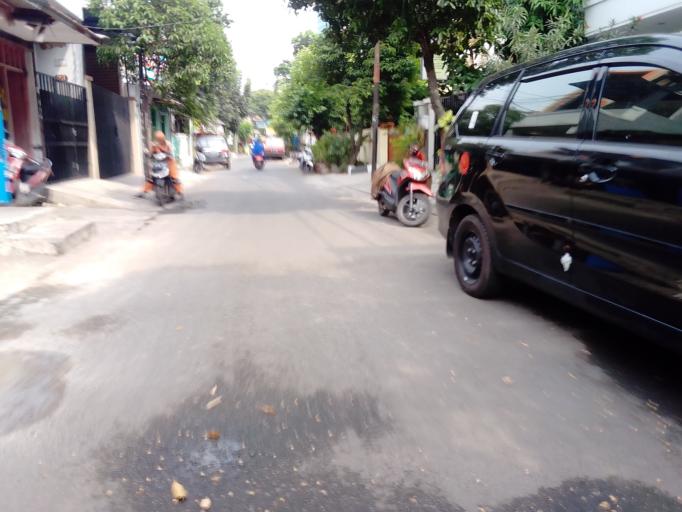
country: ID
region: Jakarta Raya
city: Jakarta
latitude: -6.2002
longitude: 106.8030
